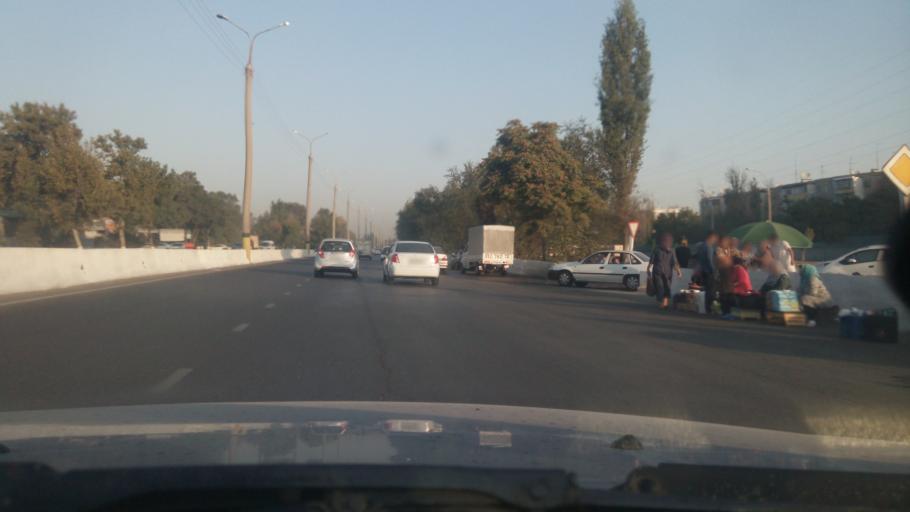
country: UZ
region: Toshkent Shahri
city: Tashkent
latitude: 41.2561
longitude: 69.1553
